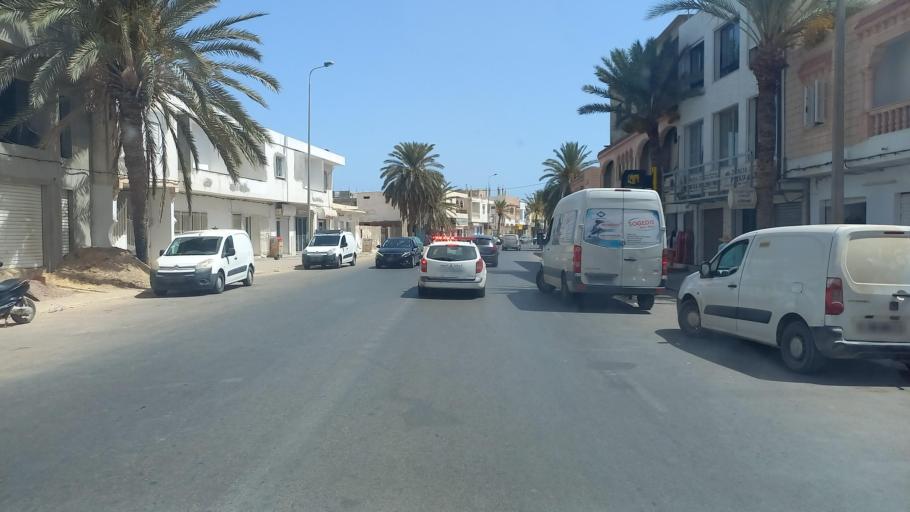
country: TN
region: Madanin
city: Zarzis
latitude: 33.5006
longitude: 11.1009
